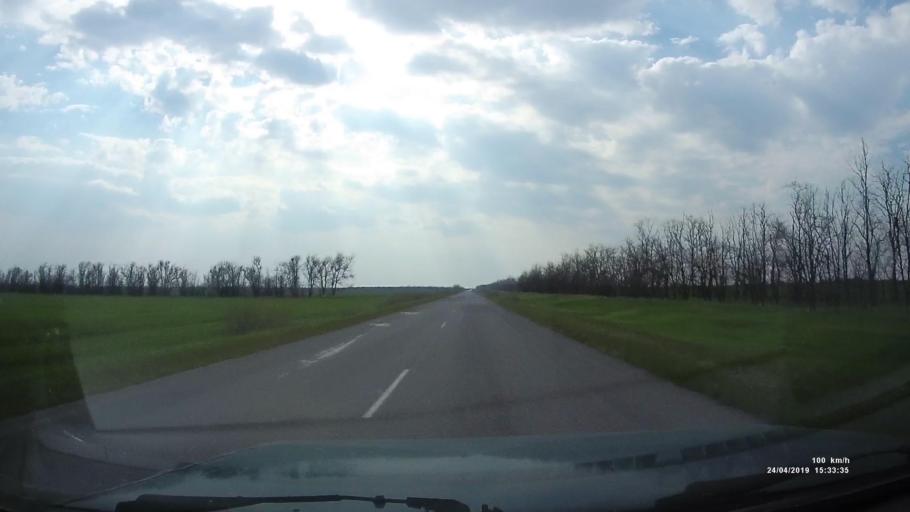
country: RU
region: Kalmykiya
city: Yashalta
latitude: 46.5996
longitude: 42.9351
